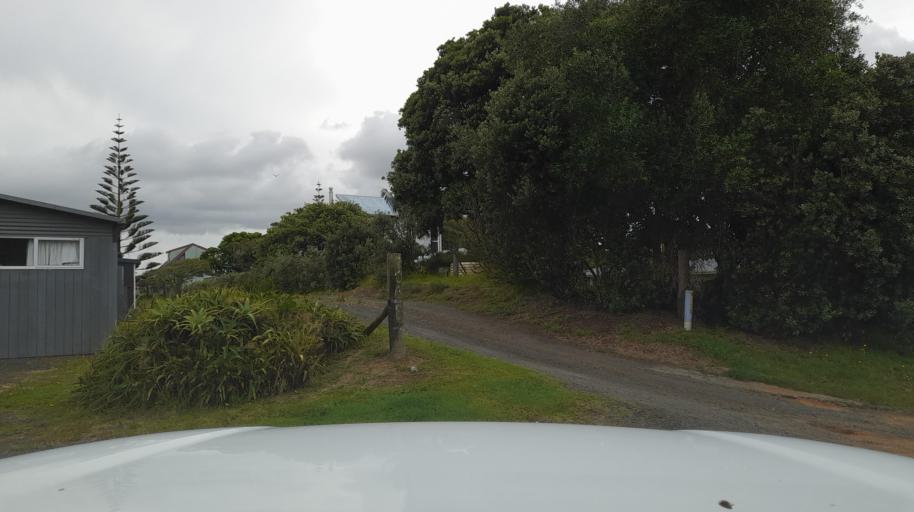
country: NZ
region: Northland
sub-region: Far North District
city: Ahipara
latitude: -35.1692
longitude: 173.1514
